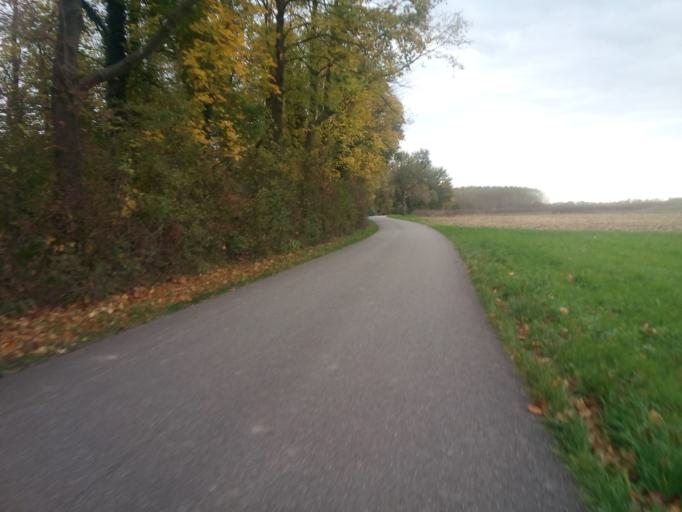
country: DE
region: Baden-Wuerttemberg
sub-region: Karlsruhe Region
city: Schwarzach
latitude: 48.7673
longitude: 8.0377
